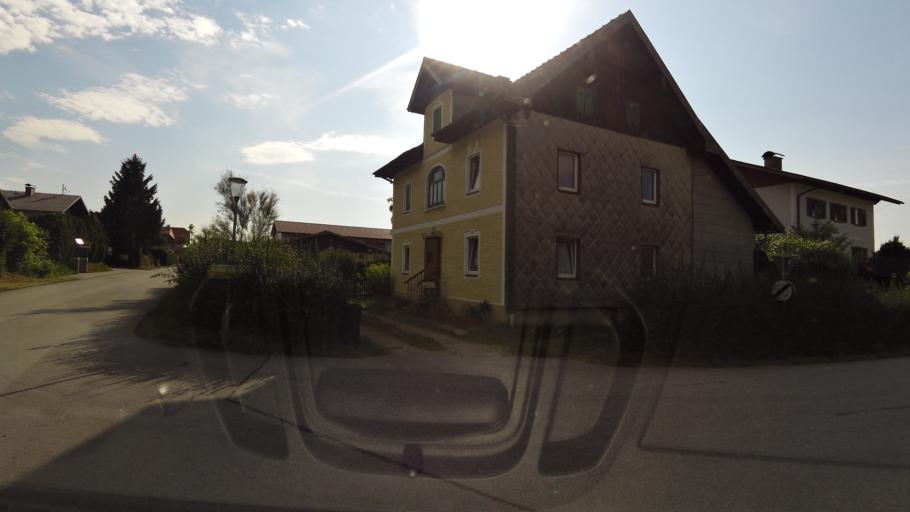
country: AT
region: Salzburg
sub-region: Politischer Bezirk Salzburg-Umgebung
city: Eugendorf
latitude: 47.8714
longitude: 13.1448
